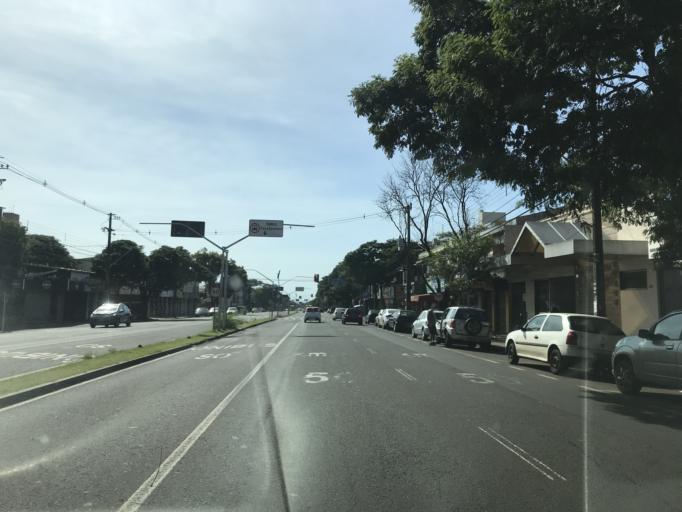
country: BR
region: Parana
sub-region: Maringa
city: Maringa
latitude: -23.4100
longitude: -51.9313
